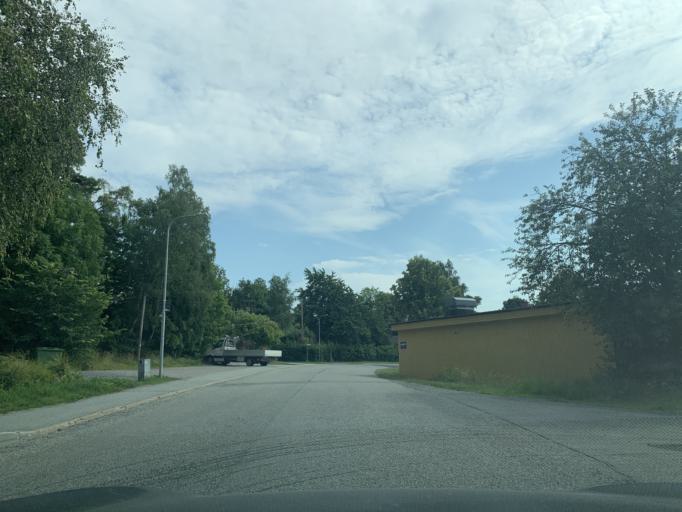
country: SE
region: Stockholm
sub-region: Norrtalje Kommun
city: Bergshamra
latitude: 59.4031
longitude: 18.0183
